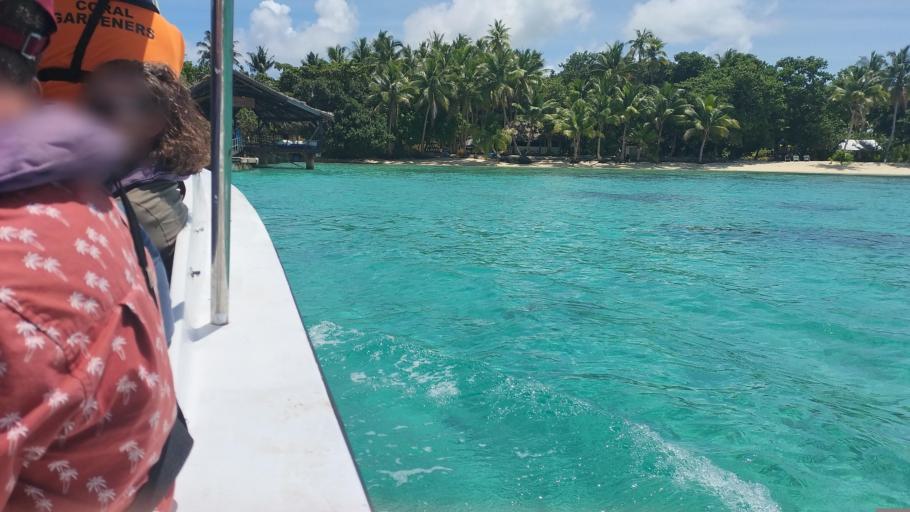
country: FJ
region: Central
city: Suva
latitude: -17.8102
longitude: 178.7211
